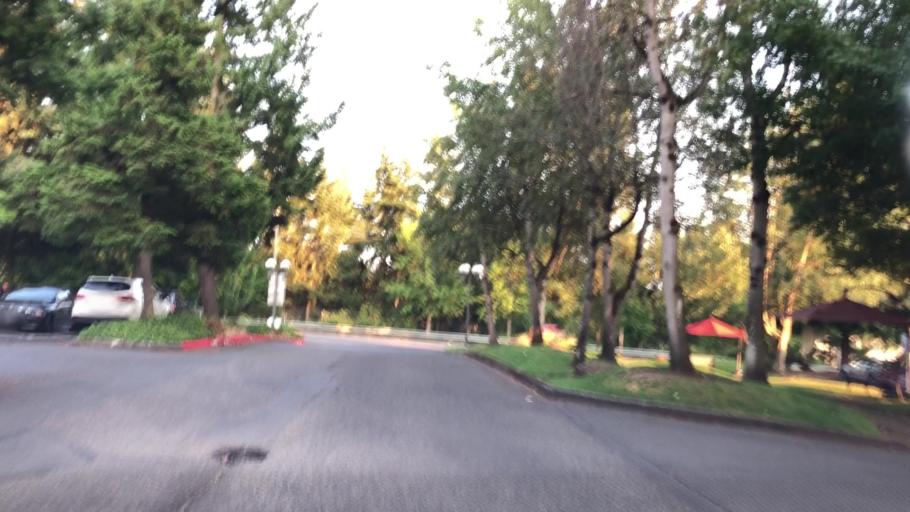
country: US
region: Washington
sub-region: King County
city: Redmond
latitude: 47.6342
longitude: -122.1464
